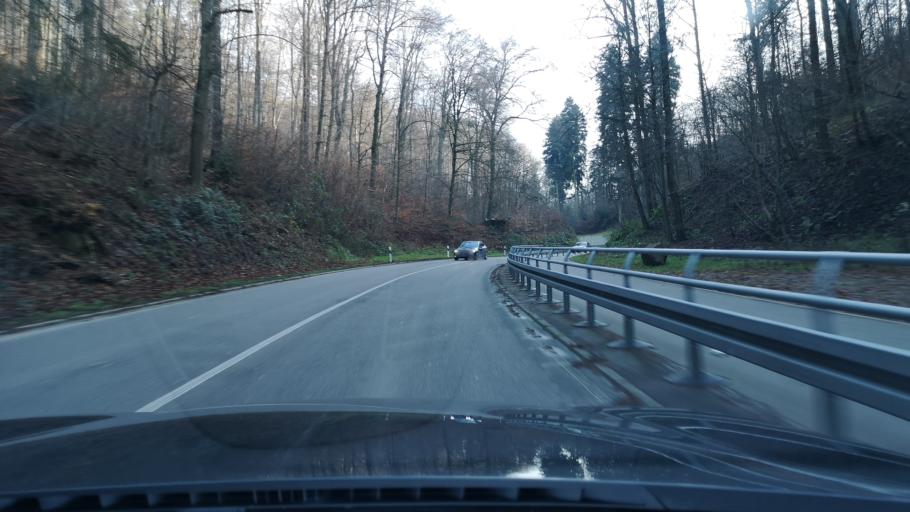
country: DE
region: Baden-Wuerttemberg
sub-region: Karlsruhe Region
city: Ettlingen
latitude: 48.9759
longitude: 8.4709
